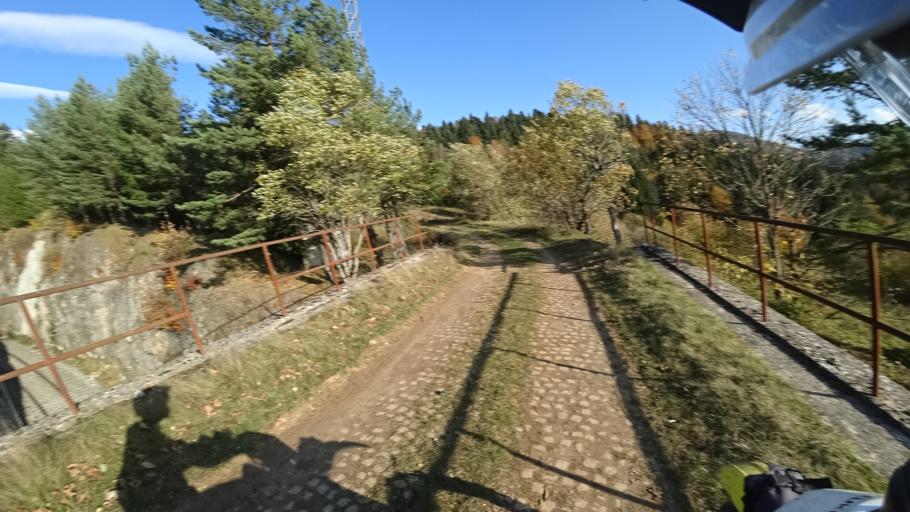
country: HR
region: Licko-Senjska
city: Jezerce
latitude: 44.9277
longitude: 15.4632
